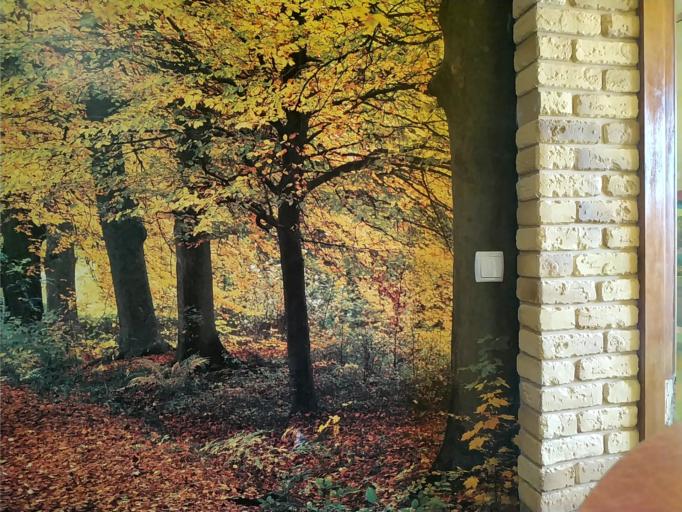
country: RU
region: Vologda
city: Nelazskoye
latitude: 59.4659
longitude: 37.6059
